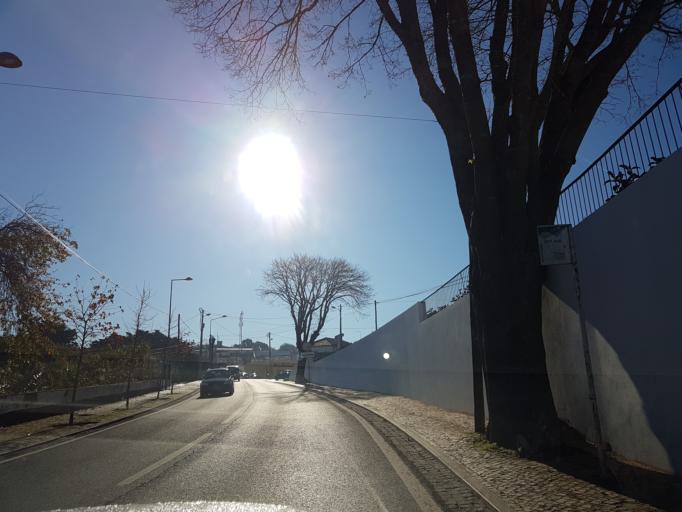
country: PT
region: Lisbon
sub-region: Sintra
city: Sintra
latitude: 38.7933
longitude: -9.3739
